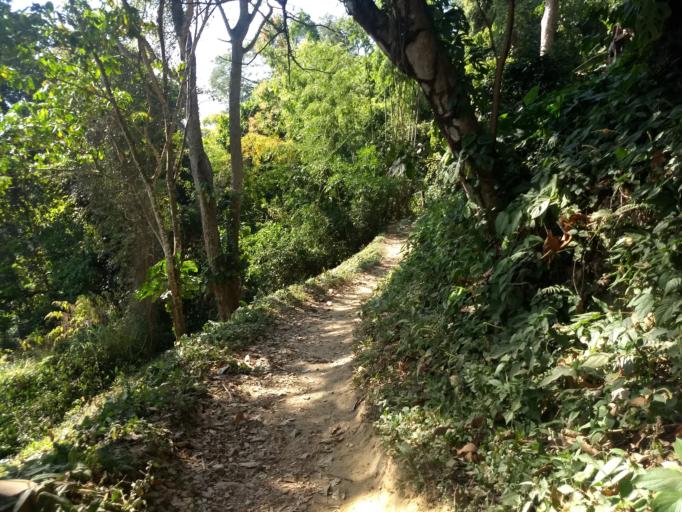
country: CO
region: Magdalena
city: Santa Marta
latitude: 11.1460
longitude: -74.1071
